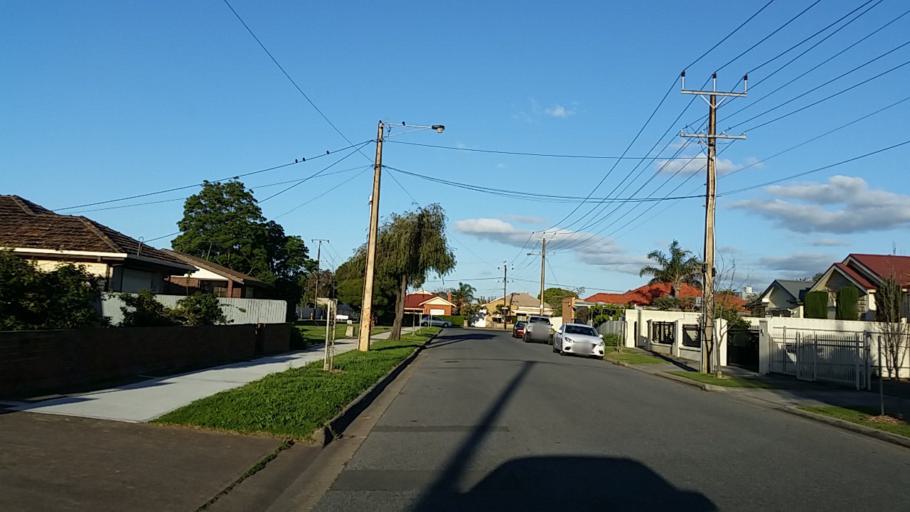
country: AU
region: South Australia
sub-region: Charles Sturt
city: Findon
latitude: -34.8921
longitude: 138.5401
